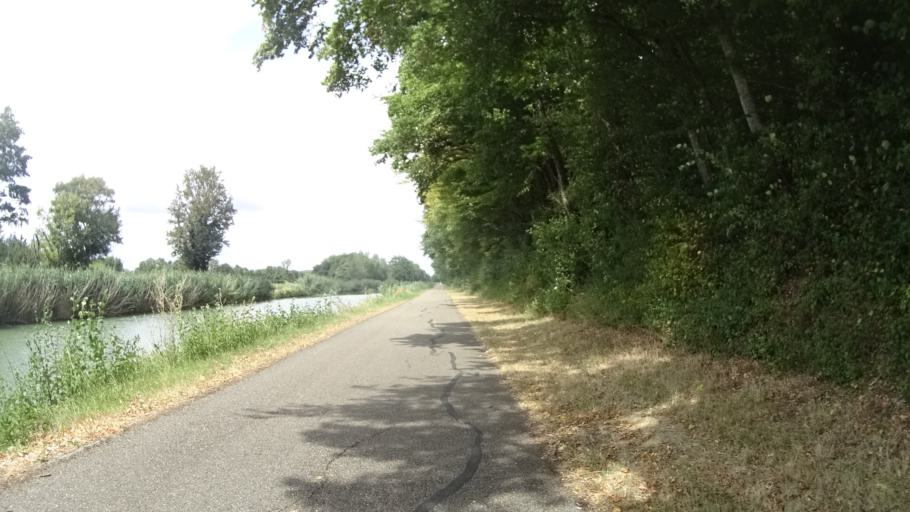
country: FR
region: Franche-Comte
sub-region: Departement du Jura
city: Damparis
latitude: 47.0761
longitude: 5.3625
